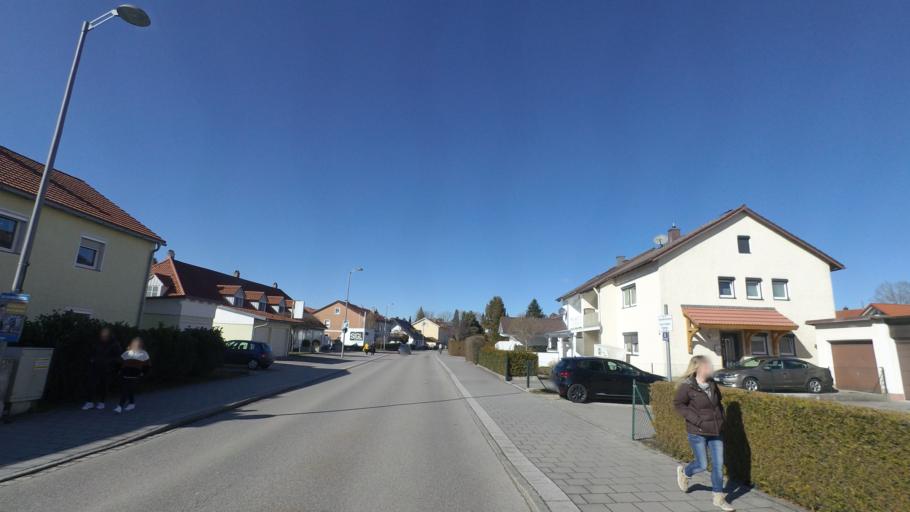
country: DE
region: Bavaria
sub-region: Upper Bavaria
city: Traunreut
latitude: 47.9606
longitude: 12.5867
